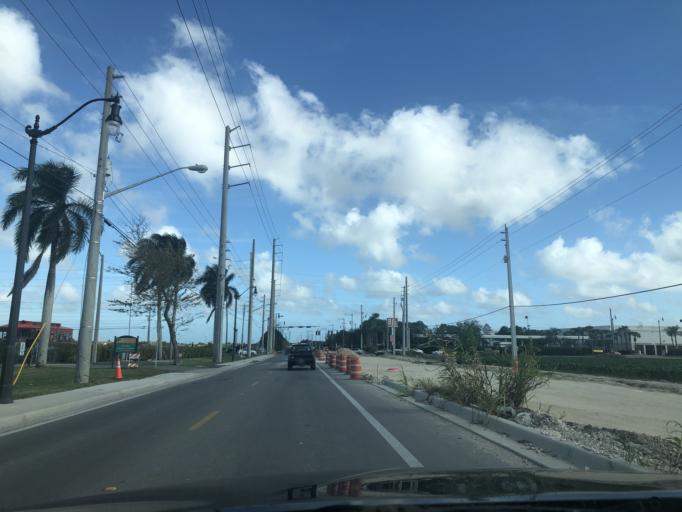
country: US
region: Florida
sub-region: Miami-Dade County
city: Homestead
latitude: 25.4625
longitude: -80.4704
